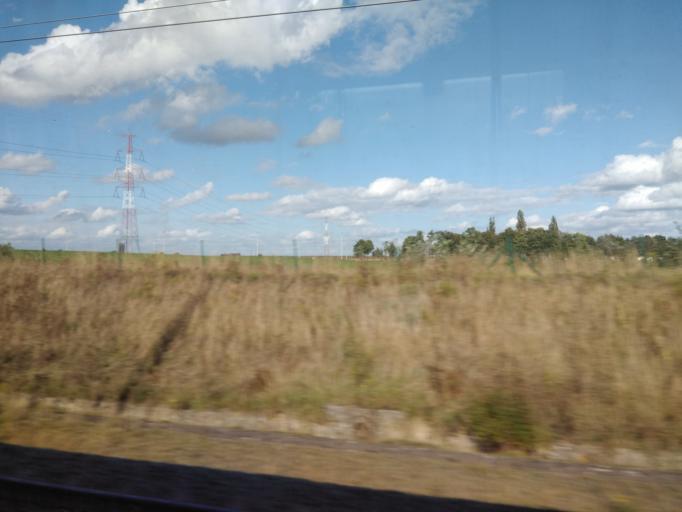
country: BE
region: Wallonia
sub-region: Province de Liege
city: Fexhe-le-Haut-Clocher
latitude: 50.6861
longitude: 5.4086
